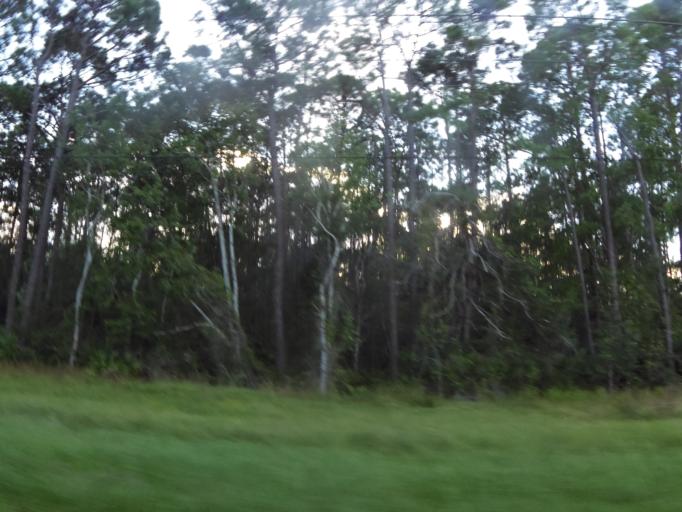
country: US
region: Georgia
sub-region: Camden County
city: St. Marys
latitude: 30.7372
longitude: -81.5480
